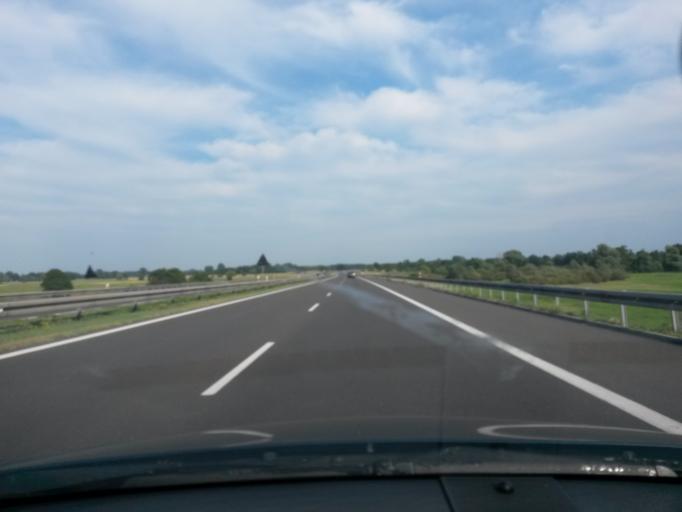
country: PL
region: Greater Poland Voivodeship
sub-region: Powiat koninski
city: Rzgow Pierwszy
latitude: 52.1947
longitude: 18.0553
